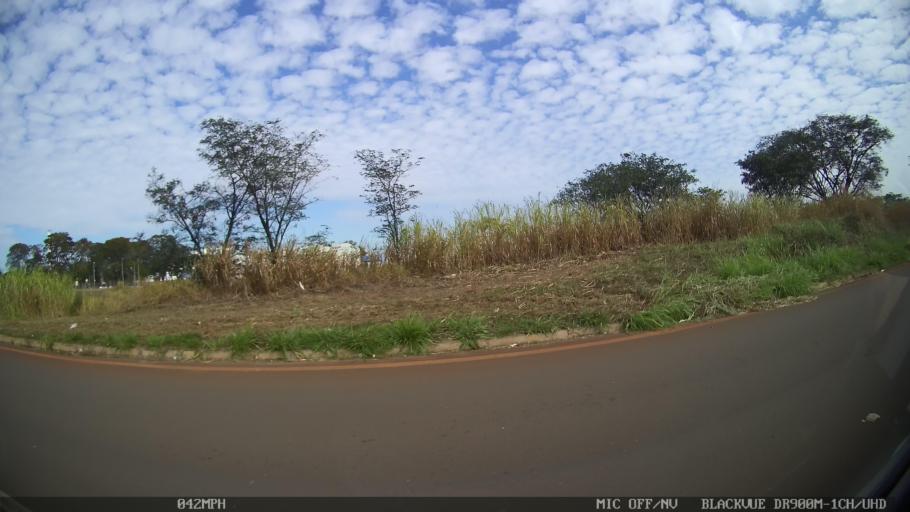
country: BR
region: Sao Paulo
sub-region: Santa Barbara D'Oeste
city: Santa Barbara d'Oeste
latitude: -22.7610
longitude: -47.4593
